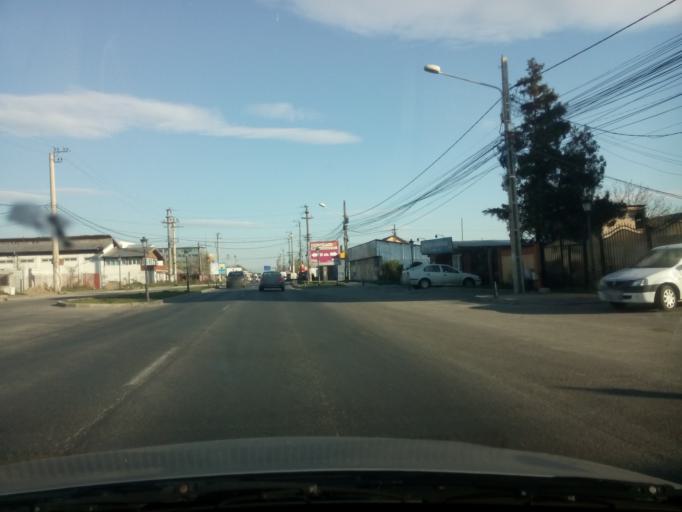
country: RO
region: Ilfov
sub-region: Comuna Mogosoaia
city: Mogosoaia
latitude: 44.5193
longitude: 26.0109
